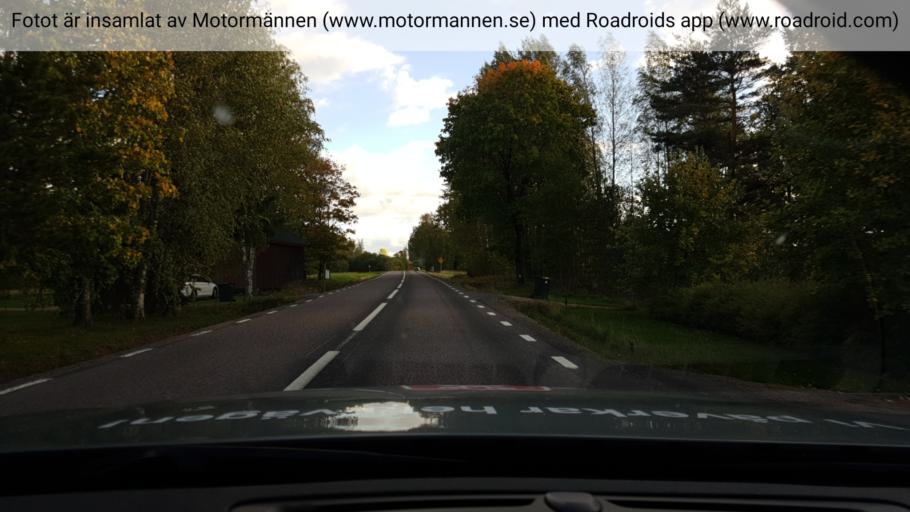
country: SE
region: Vaermland
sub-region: Karlstads Kommun
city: Molkom
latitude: 59.7023
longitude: 13.6809
